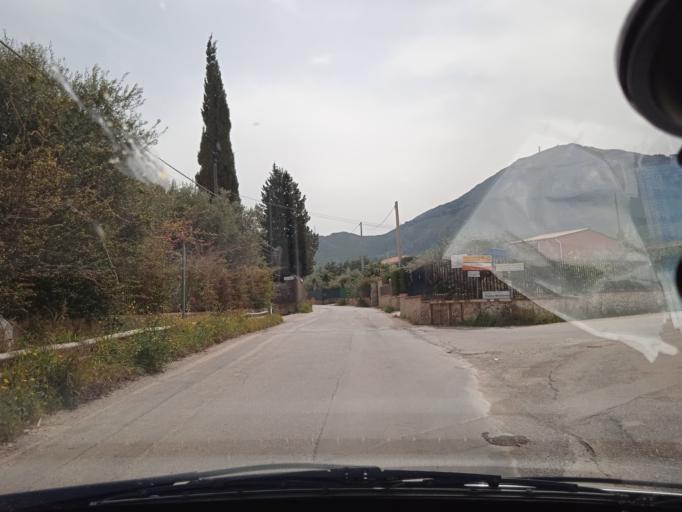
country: IT
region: Sicily
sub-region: Palermo
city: Torre Colonna-Sperone
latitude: 38.0334
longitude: 13.5646
